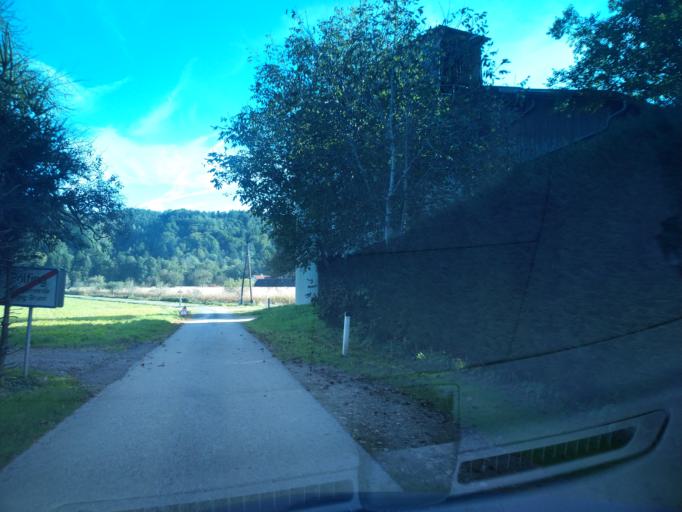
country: AT
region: Styria
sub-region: Politischer Bezirk Deutschlandsberg
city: Sankt Martin im Sulmtal
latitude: 46.7319
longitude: 15.3111
